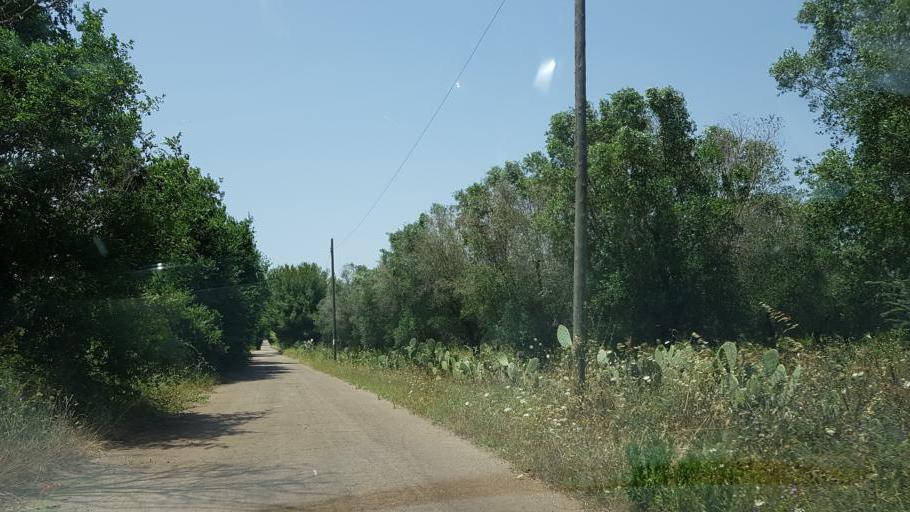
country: IT
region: Apulia
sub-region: Provincia di Lecce
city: Porto Cesareo
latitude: 40.3257
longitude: 17.8610
